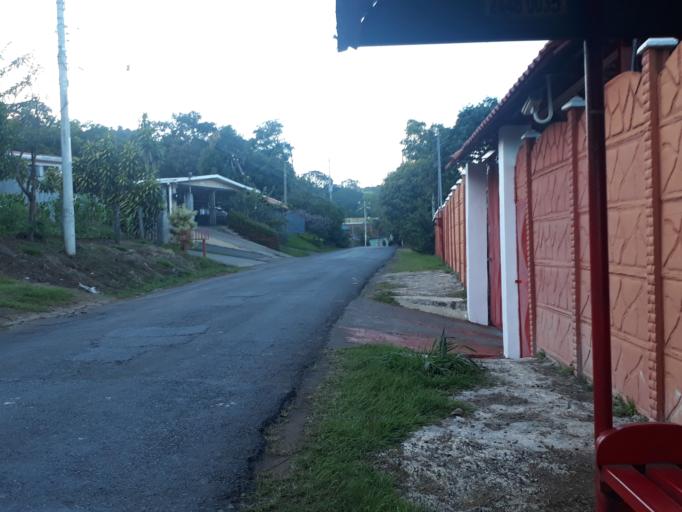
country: CR
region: Alajuela
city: Carrillos
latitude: 10.0397
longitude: -84.3284
